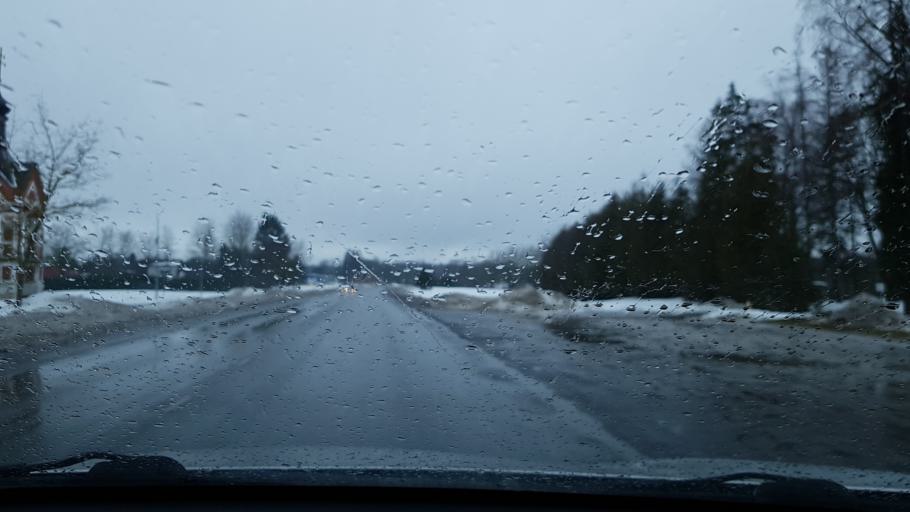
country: EE
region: Raplamaa
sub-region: Kohila vald
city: Kohila
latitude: 59.1698
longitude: 24.7644
